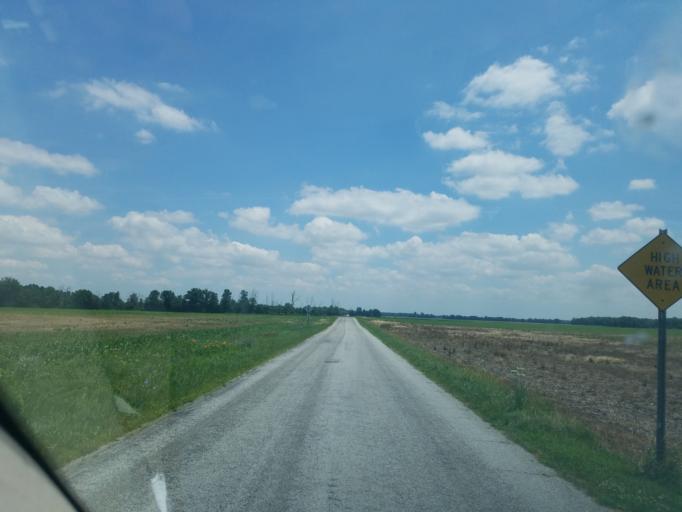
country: US
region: Ohio
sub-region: Hancock County
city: Arlington
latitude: 40.7756
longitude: -83.6377
